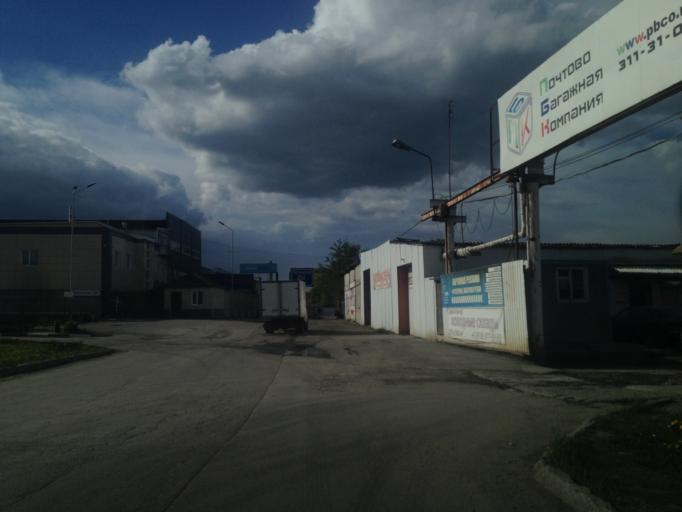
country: RU
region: Sverdlovsk
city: Yekaterinburg
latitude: 56.8686
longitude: 60.5861
